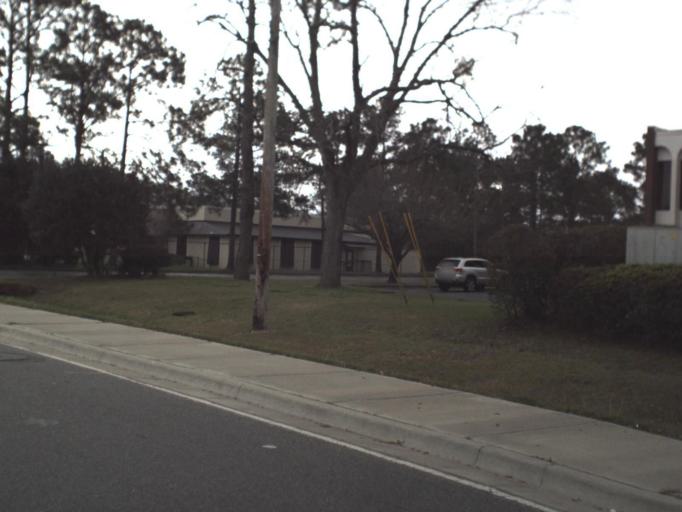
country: US
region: Florida
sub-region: Leon County
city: Tallahassee
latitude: 30.4270
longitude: -84.2346
